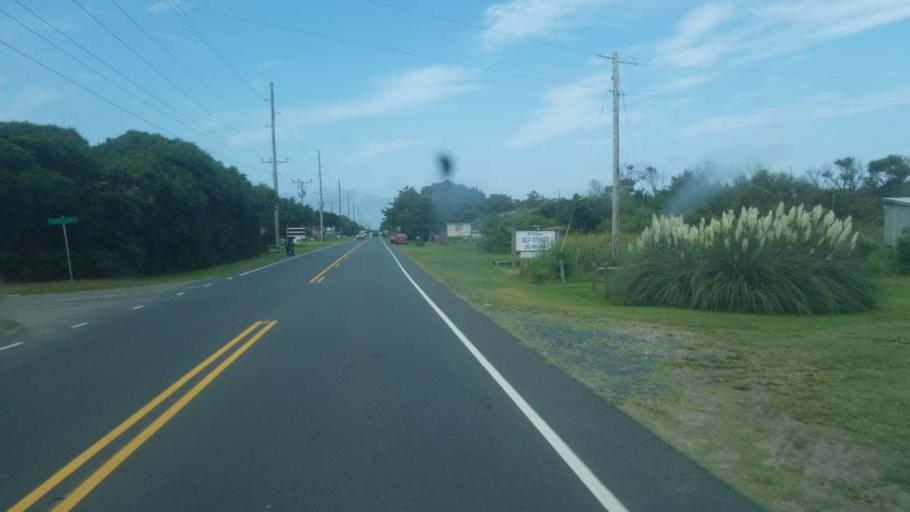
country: US
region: North Carolina
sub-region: Dare County
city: Buxton
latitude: 35.2345
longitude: -75.6243
